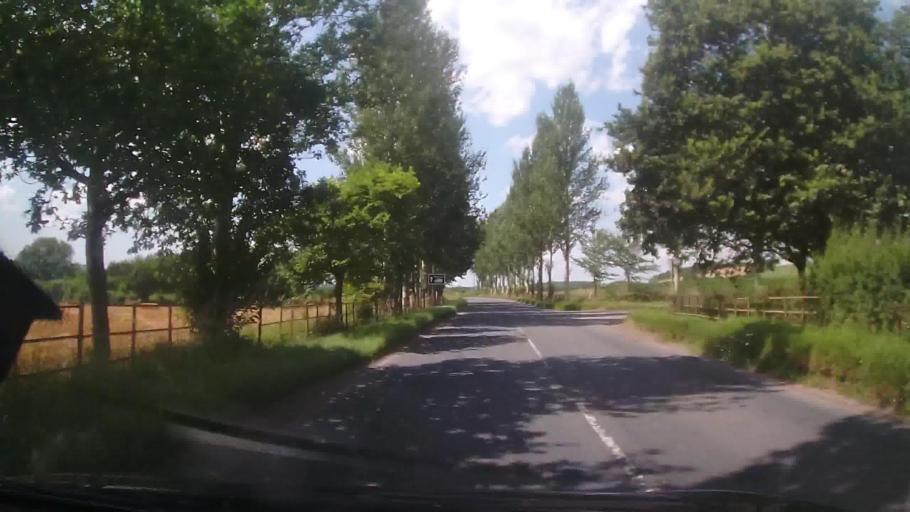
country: GB
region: England
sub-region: Herefordshire
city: Bodenham
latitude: 52.1522
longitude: -2.6480
